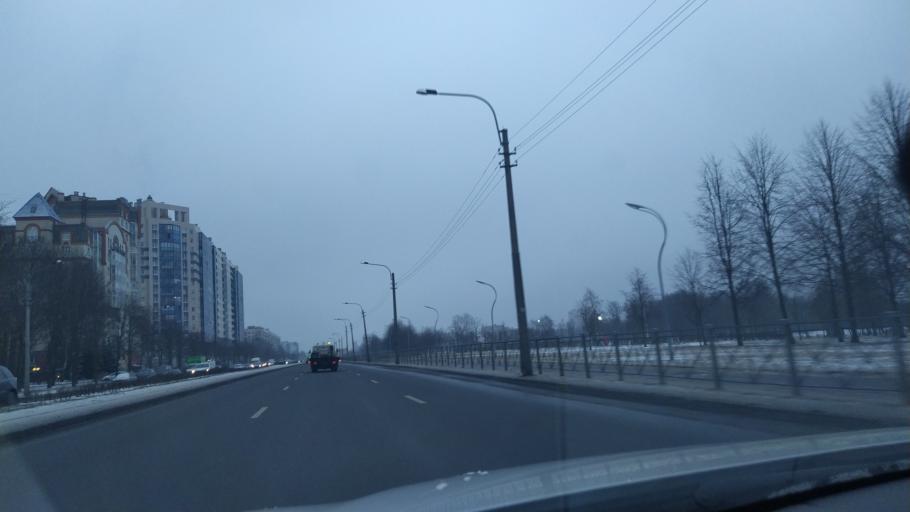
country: RU
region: St.-Petersburg
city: Grazhdanka
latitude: 60.0297
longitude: 30.3960
